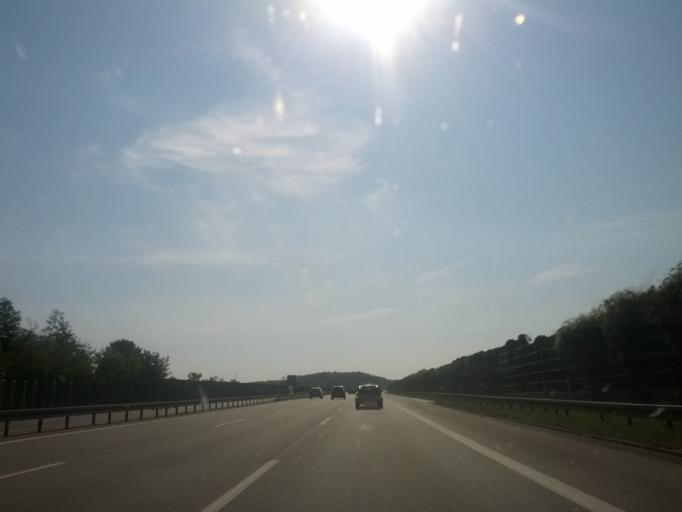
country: DE
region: Brandenburg
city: Woltersdorf
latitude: 52.4703
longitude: 13.7754
